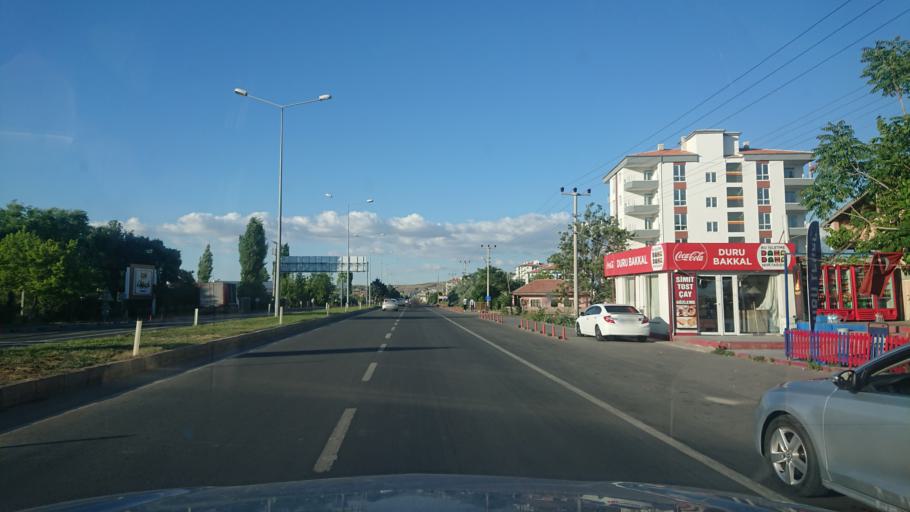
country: TR
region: Aksaray
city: Aksaray
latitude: 38.3851
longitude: 33.9955
